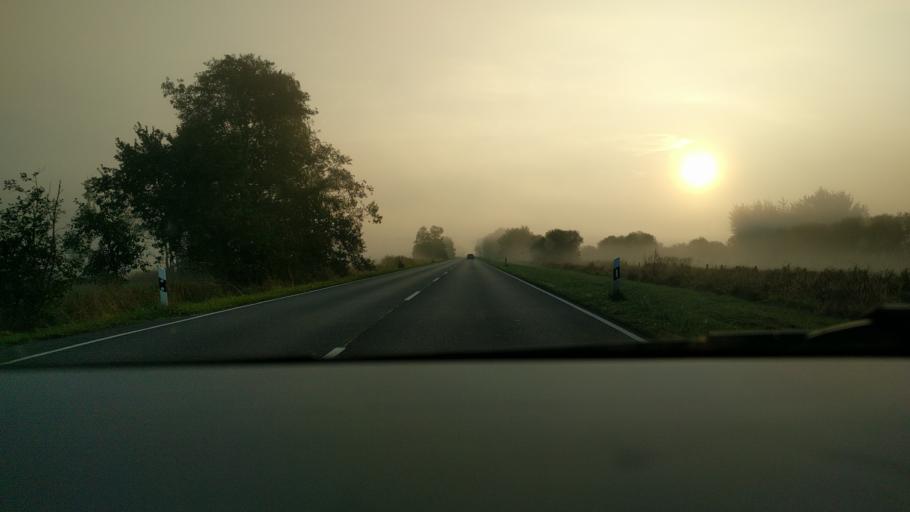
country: DE
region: Lower Saxony
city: Osloss
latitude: 52.4373
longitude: 10.6894
